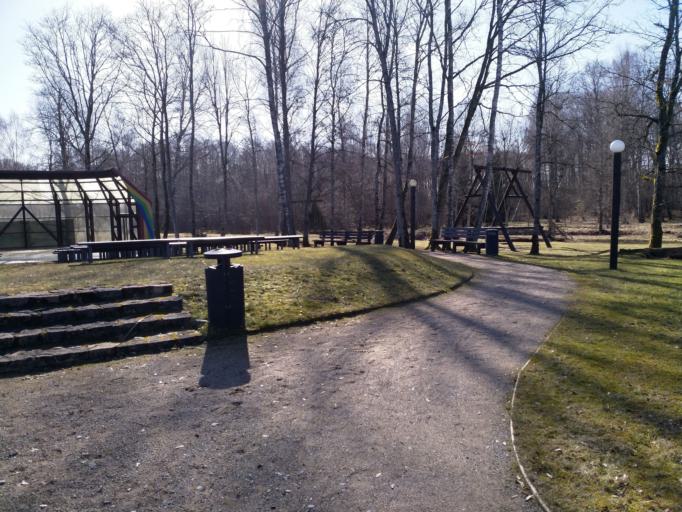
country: LV
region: Aizpute
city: Aizpute
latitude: 56.8325
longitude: 21.7752
